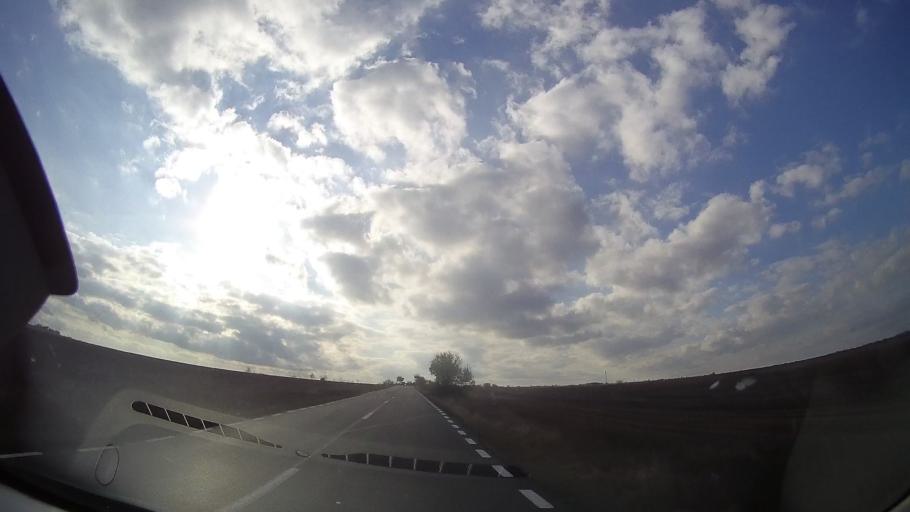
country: RO
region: Constanta
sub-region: Comuna Albesti
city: Albesti
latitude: 43.8168
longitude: 28.4596
